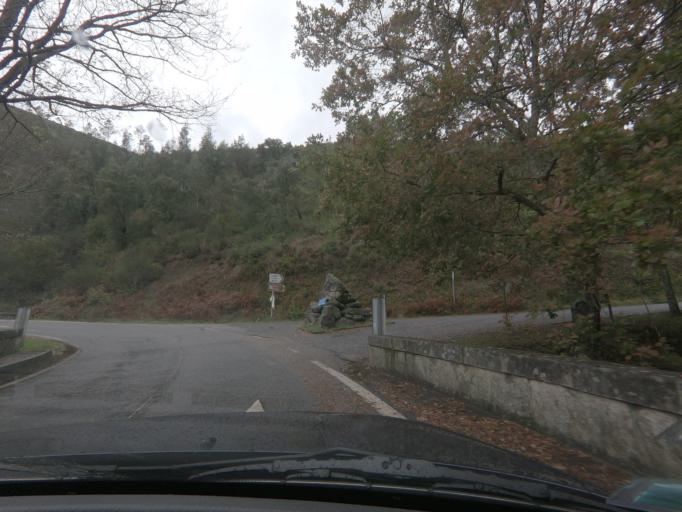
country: PT
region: Vila Real
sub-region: Mondim de Basto
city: Mondim de Basto
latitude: 41.3552
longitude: -7.8812
